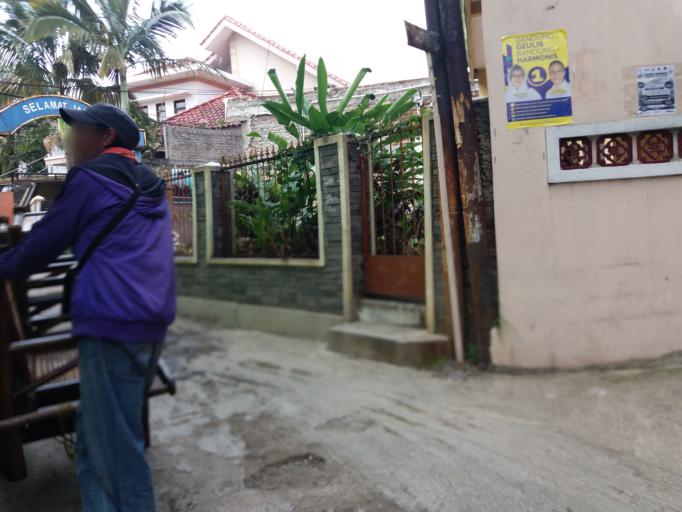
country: ID
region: West Java
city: Bandung
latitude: -6.9177
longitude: 107.6519
